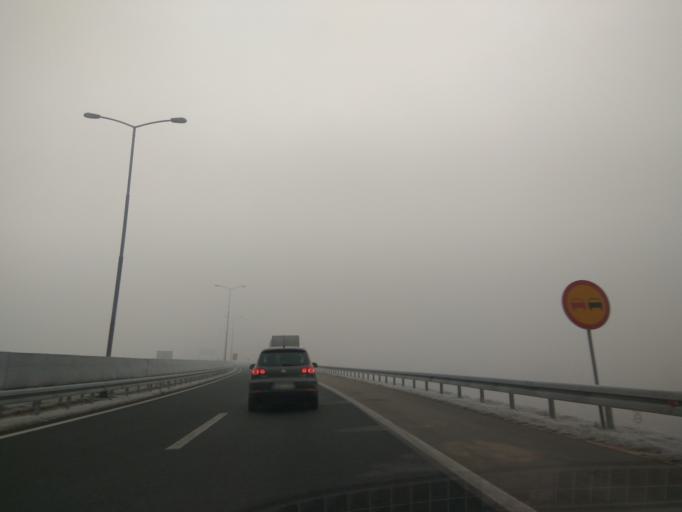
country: BA
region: Federation of Bosnia and Herzegovina
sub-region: Kanton Sarajevo
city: Sarajevo
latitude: 43.8528
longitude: 18.3146
